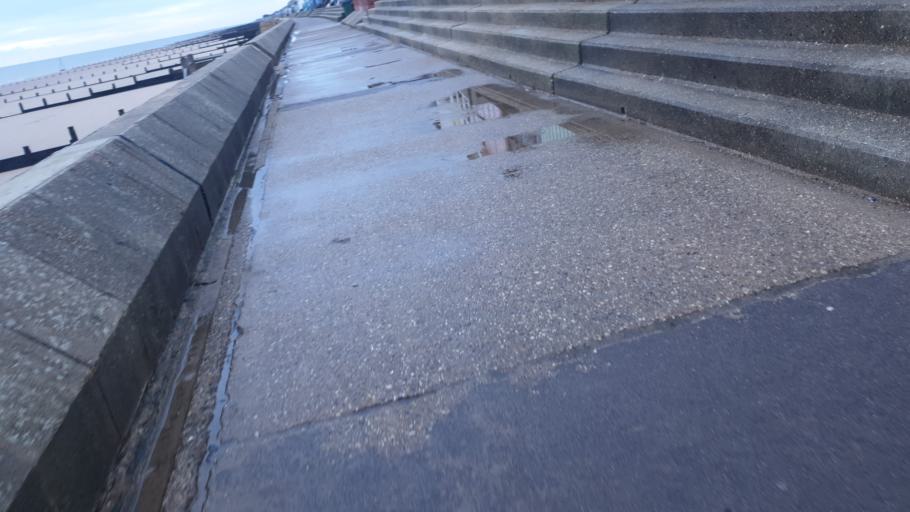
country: GB
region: England
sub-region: Essex
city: Frinton-on-Sea
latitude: 51.8337
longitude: 1.2541
